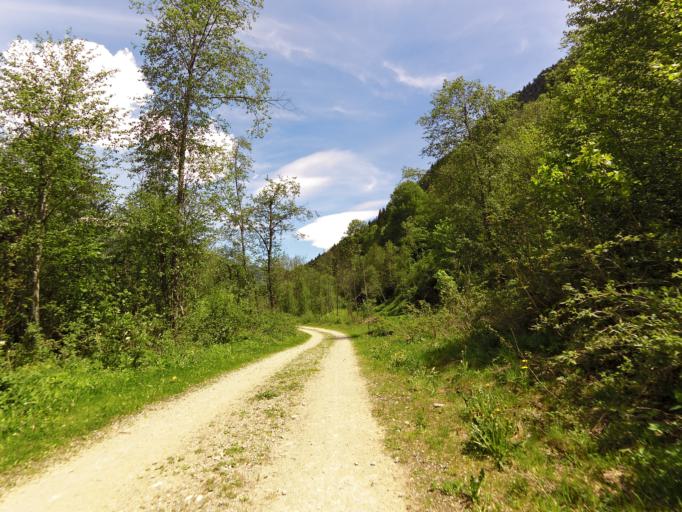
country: CH
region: Grisons
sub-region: Surselva District
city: Trun
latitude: 46.7255
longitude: 8.9601
